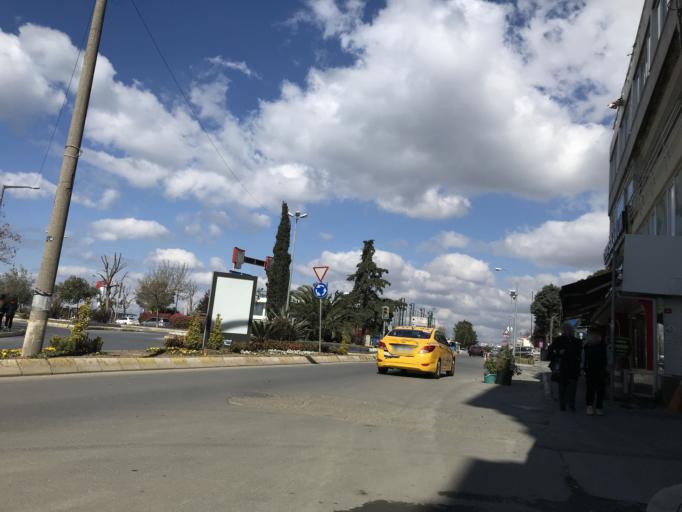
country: TR
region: Istanbul
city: Maltepe
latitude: 40.9231
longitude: 29.1272
